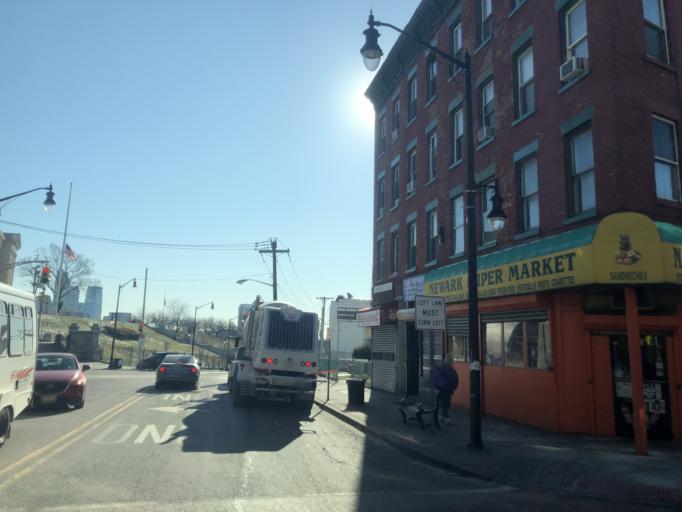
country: US
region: New Jersey
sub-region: Hudson County
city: Jersey City
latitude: 40.7304
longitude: -74.0556
